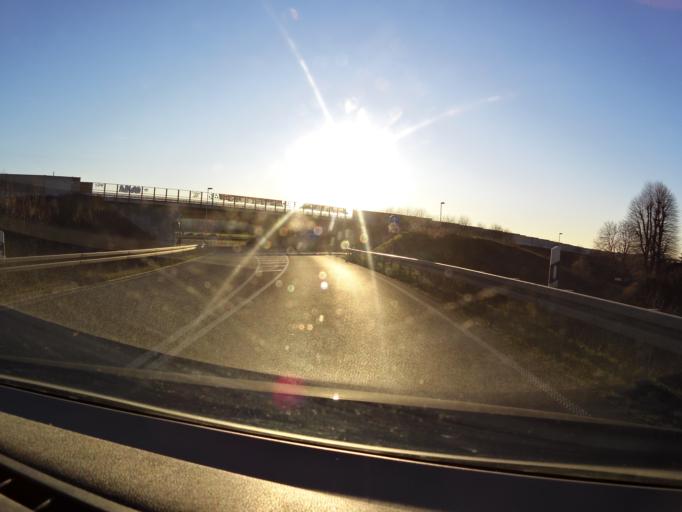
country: NL
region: Limburg
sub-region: Gemeente Venlo
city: Venlo
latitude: 51.3353
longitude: 6.1959
